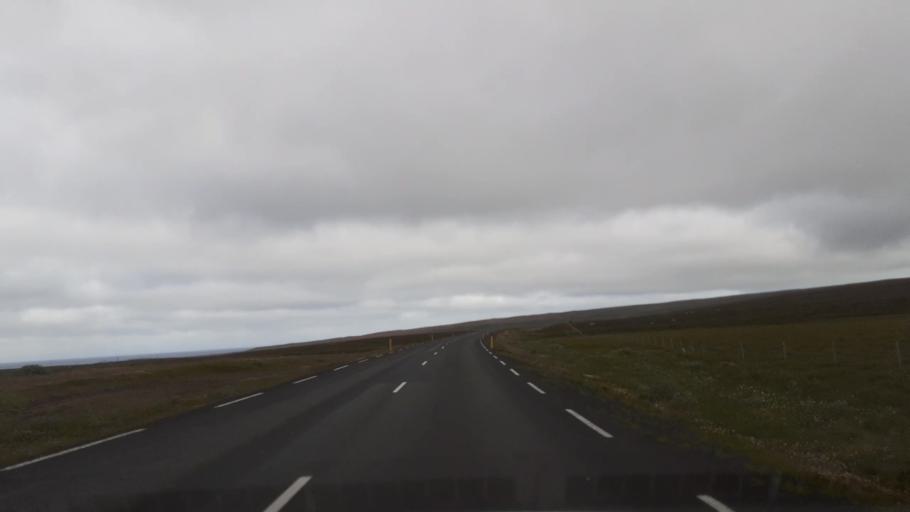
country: IS
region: Northeast
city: Husavik
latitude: 66.1708
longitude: -17.2094
